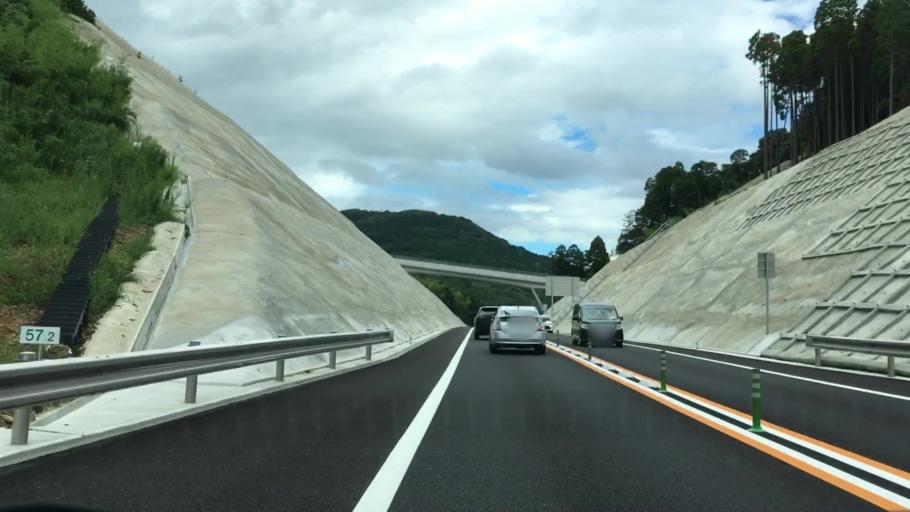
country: JP
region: Saga Prefecture
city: Imaricho-ko
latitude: 33.3052
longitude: 129.9160
